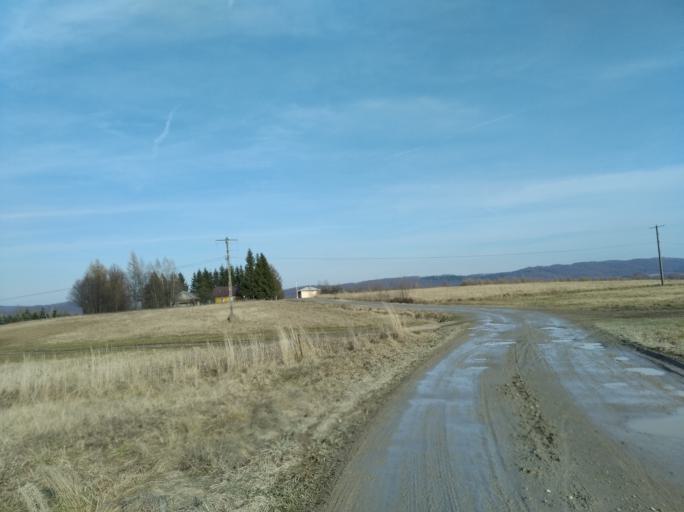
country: PL
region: Subcarpathian Voivodeship
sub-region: Powiat brzozowski
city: Gorki
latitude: 49.6478
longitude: 22.0599
